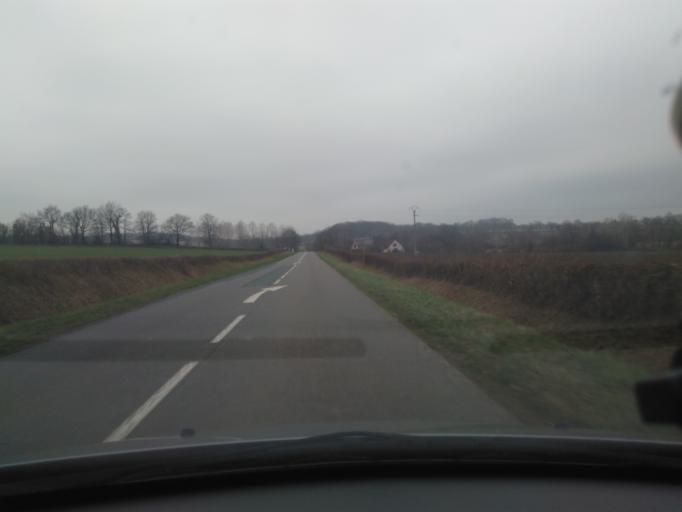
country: FR
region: Centre
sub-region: Departement du Cher
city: Chateaumeillant
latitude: 46.6355
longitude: 2.1922
